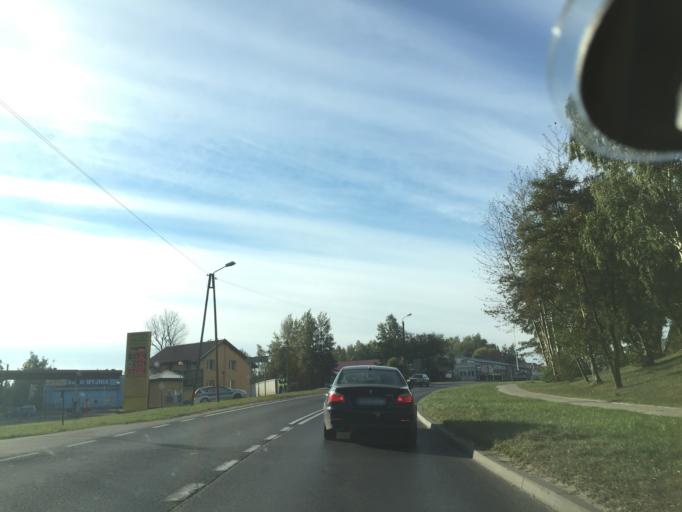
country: PL
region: Warmian-Masurian Voivodeship
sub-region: Powiat lidzbarski
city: Lidzbark Warminski
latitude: 54.1181
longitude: 20.5731
